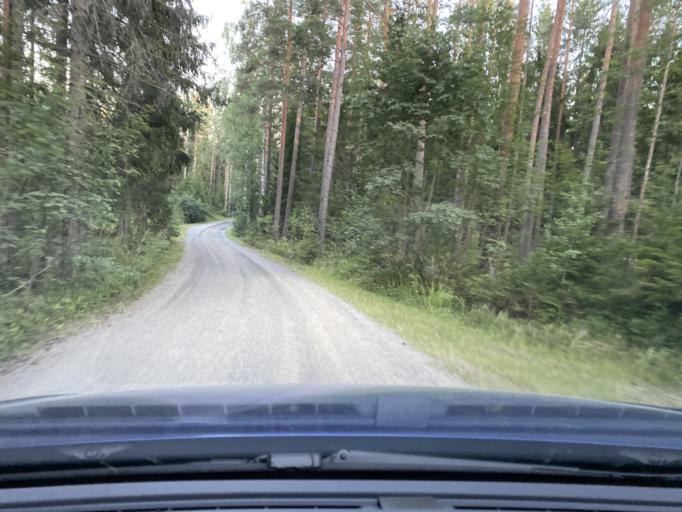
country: FI
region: Satakunta
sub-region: Rauma
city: Kiukainen
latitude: 61.1437
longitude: 22.0225
